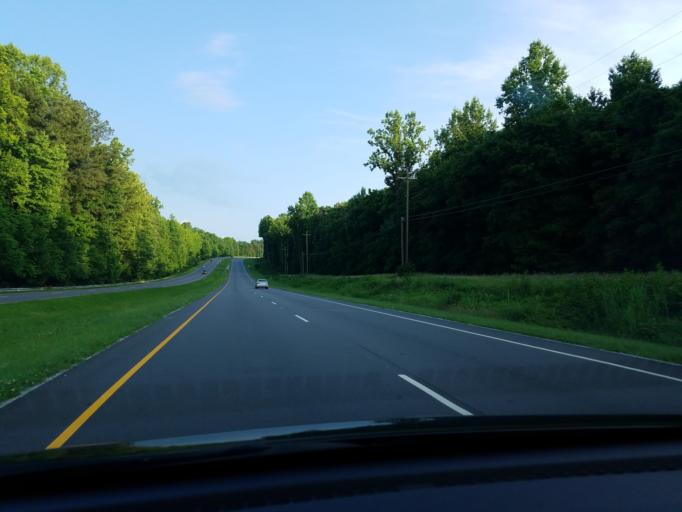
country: US
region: North Carolina
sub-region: Durham County
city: Gorman
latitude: 36.1314
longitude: -78.9037
